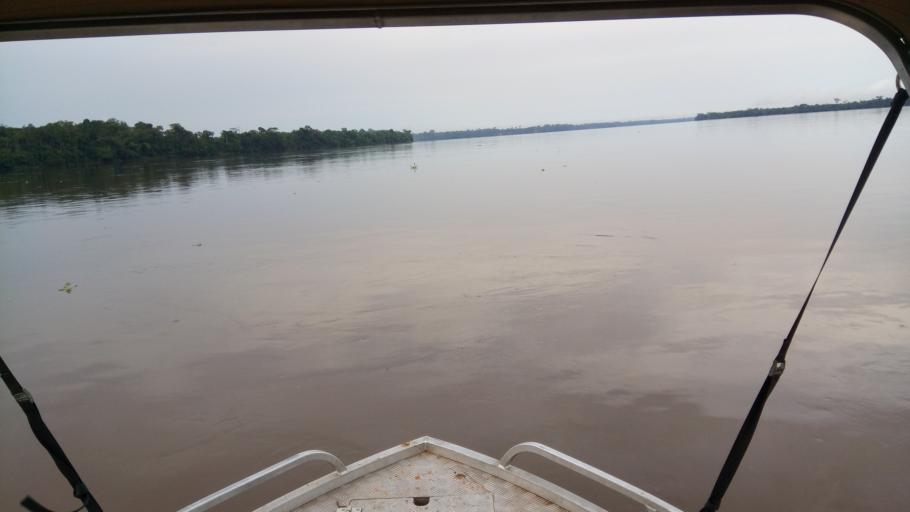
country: CD
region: Eastern Province
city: Kisangani
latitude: 0.5738
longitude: 24.8009
